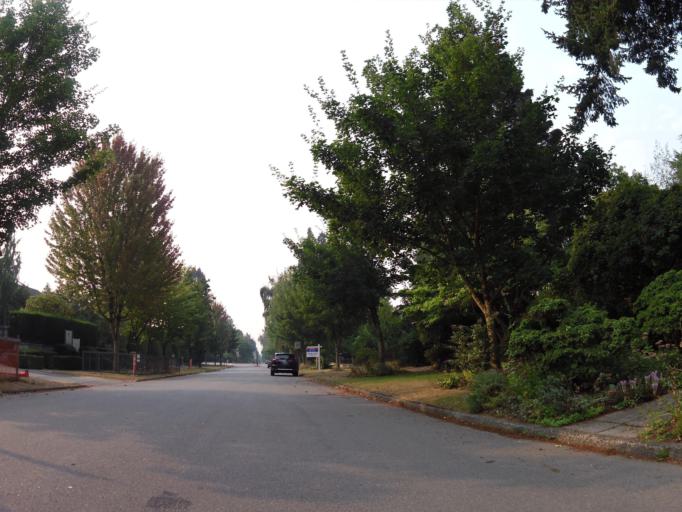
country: CA
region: British Columbia
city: Vancouver
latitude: 49.2356
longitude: -123.1477
